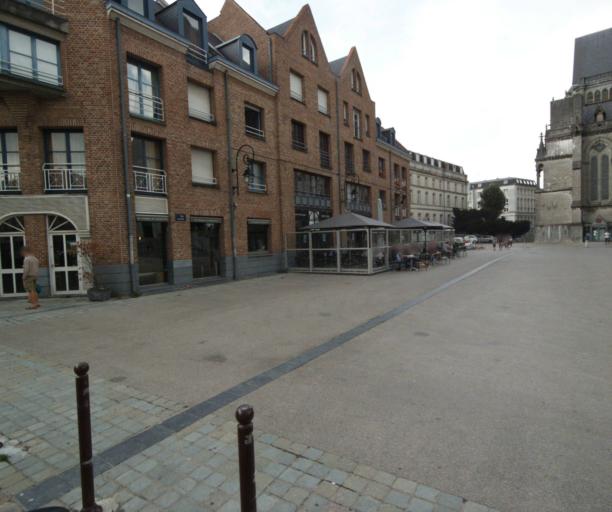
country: FR
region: Nord-Pas-de-Calais
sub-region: Departement du Nord
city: Lille
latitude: 50.6399
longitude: 3.0615
